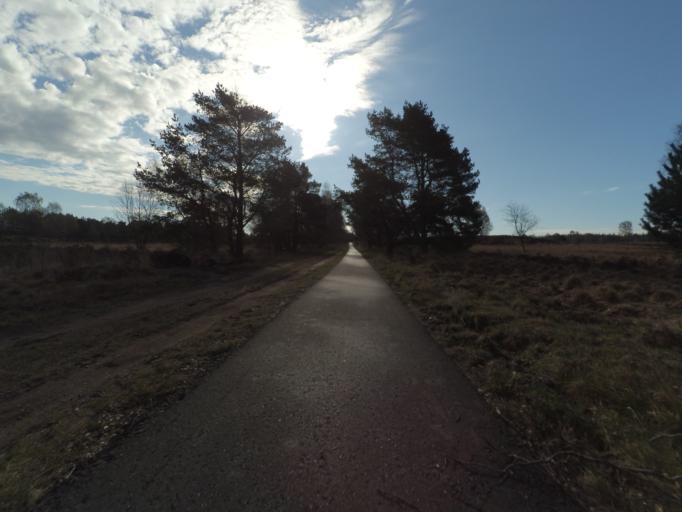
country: NL
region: Gelderland
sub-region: Gemeente Apeldoorn
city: Uddel
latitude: 52.2000
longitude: 5.8586
